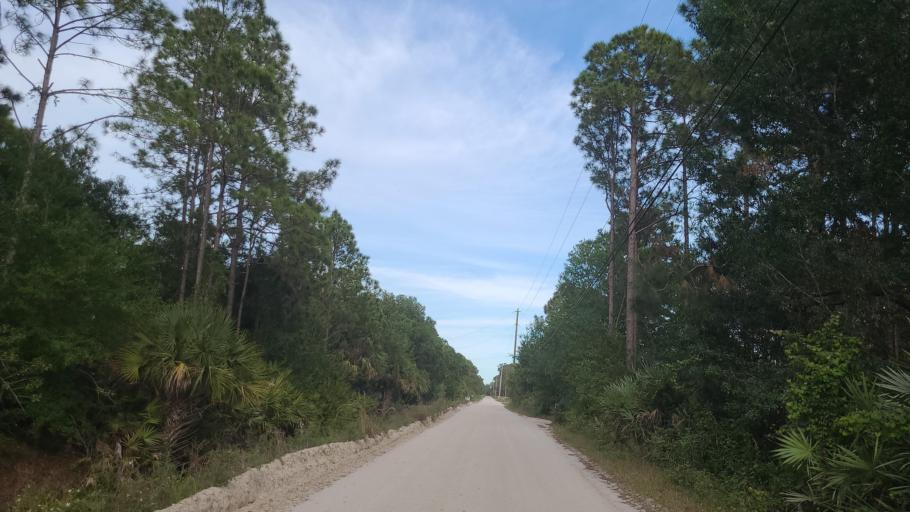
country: US
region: Florida
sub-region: Indian River County
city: Fellsmere
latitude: 27.7464
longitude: -80.5882
